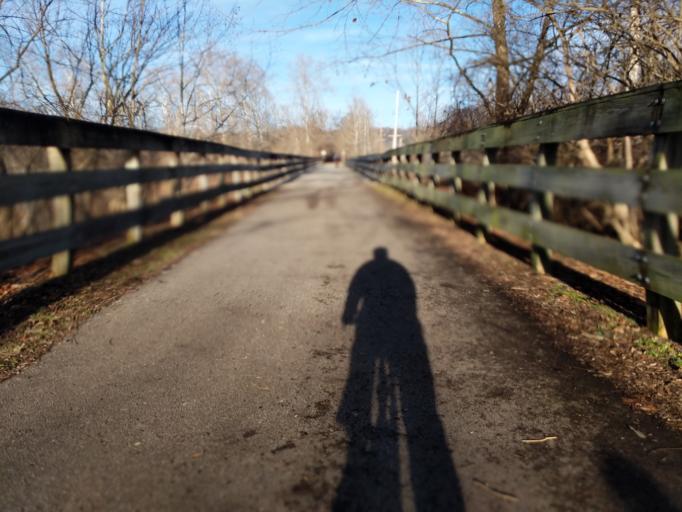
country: US
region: Ohio
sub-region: Athens County
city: Athens
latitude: 39.3405
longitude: -82.1095
